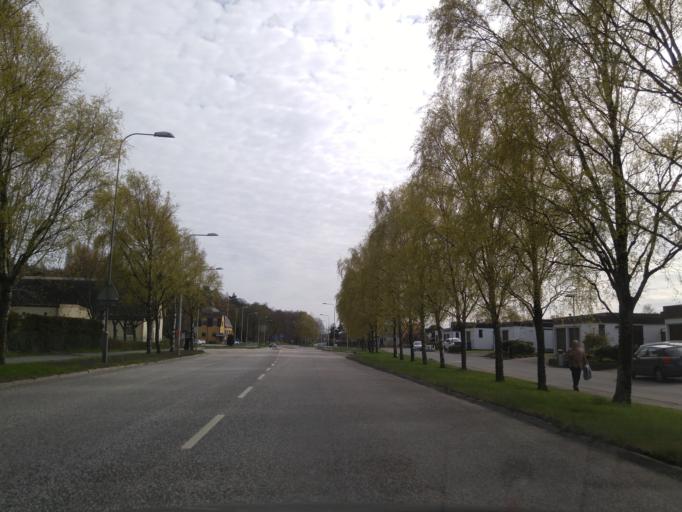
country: SE
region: Vaestra Goetaland
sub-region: Goteborg
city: Majorna
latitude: 57.6612
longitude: 11.8725
